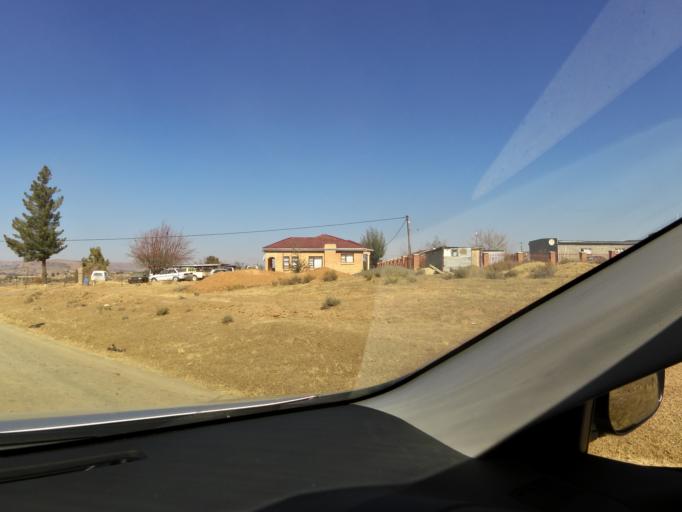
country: LS
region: Maseru
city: Maseru
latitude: -29.4373
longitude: 27.5647
